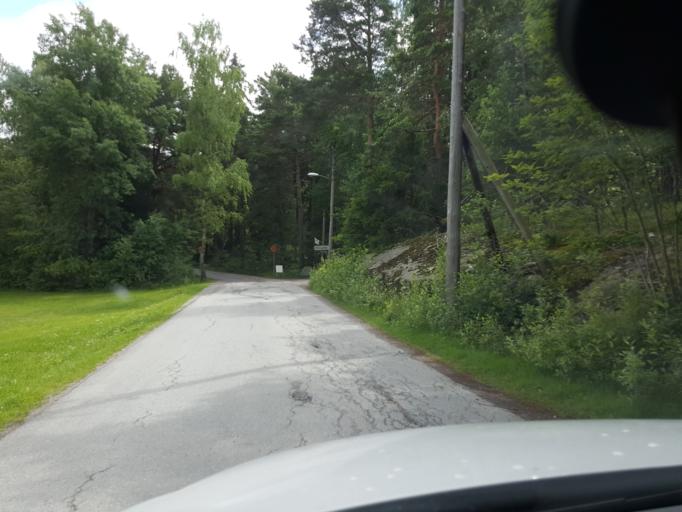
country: SE
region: Stockholm
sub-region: Stockholms Kommun
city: Bromma
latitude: 59.3166
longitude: 17.9604
